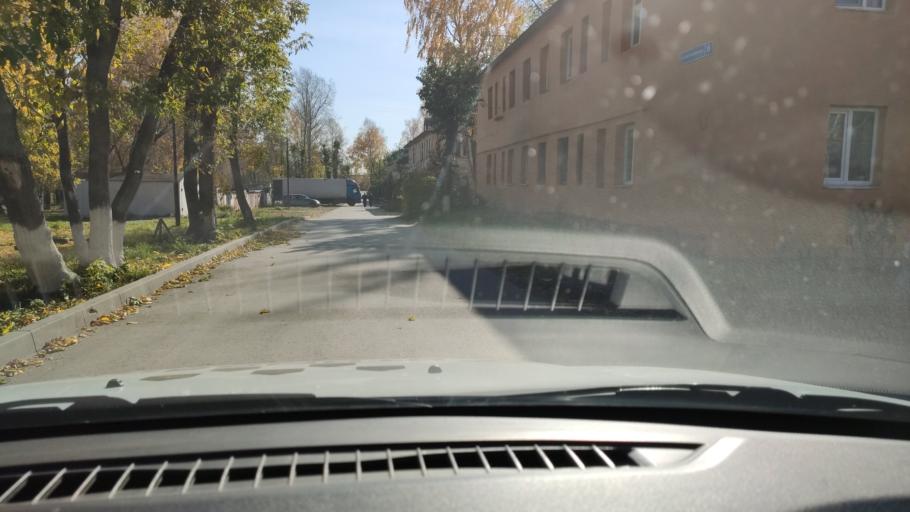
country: RU
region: Perm
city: Kondratovo
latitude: 57.9518
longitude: 56.1146
